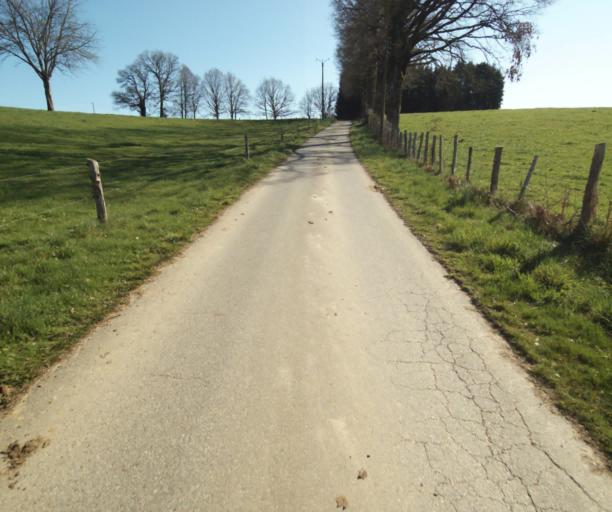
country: FR
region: Limousin
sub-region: Departement de la Correze
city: Chamboulive
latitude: 45.4787
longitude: 1.7365
